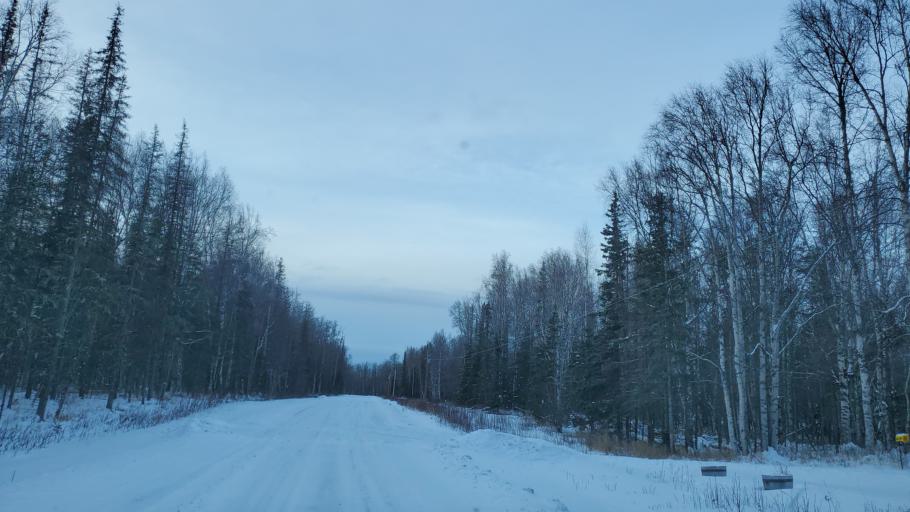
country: US
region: Alaska
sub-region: Matanuska-Susitna Borough
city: Lakes
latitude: 61.6717
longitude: -149.2785
